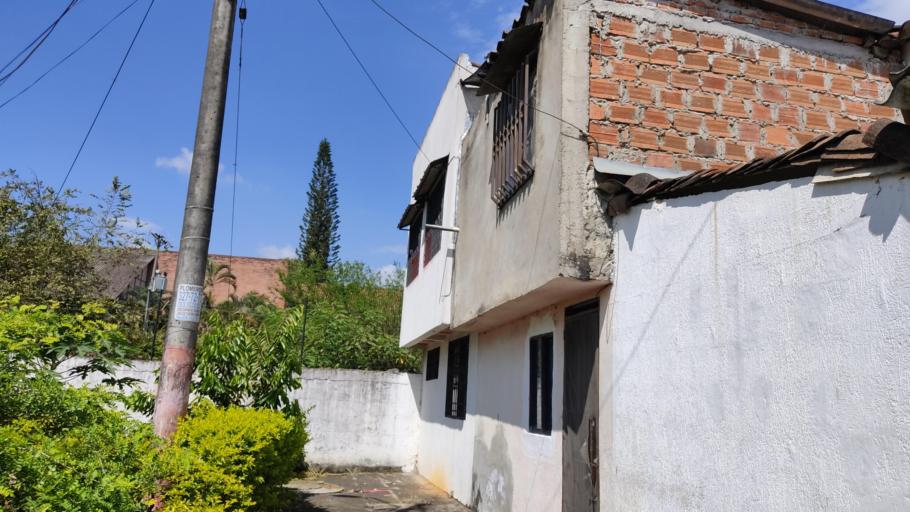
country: CO
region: Valle del Cauca
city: Jamundi
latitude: 3.2545
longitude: -76.5456
